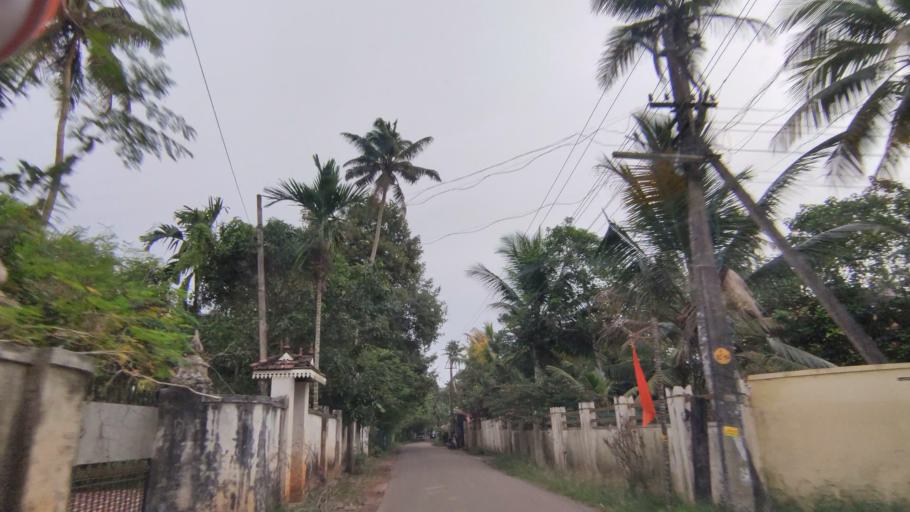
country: IN
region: Kerala
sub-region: Alappuzha
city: Shertallai
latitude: 9.6639
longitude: 76.3647
